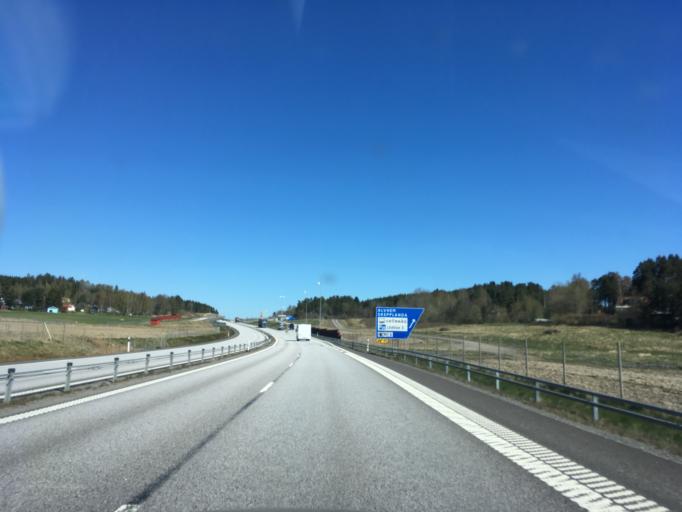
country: SE
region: Vaestra Goetaland
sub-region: Ale Kommun
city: Skepplanda
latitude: 57.9823
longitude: 12.1623
